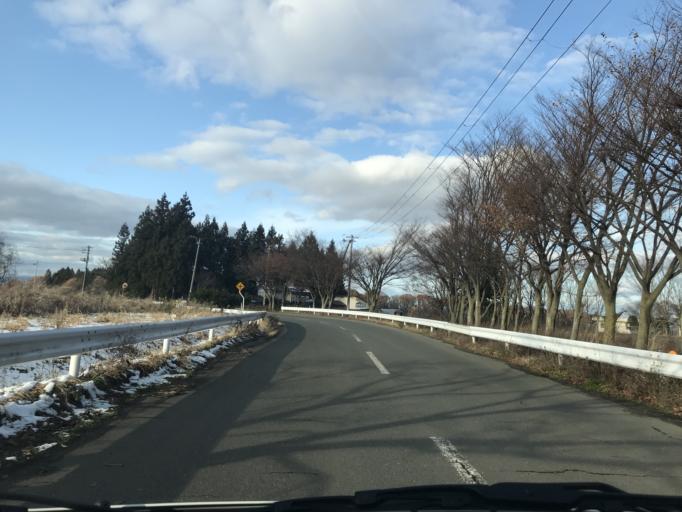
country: JP
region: Iwate
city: Kitakami
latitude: 39.2544
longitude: 141.0324
